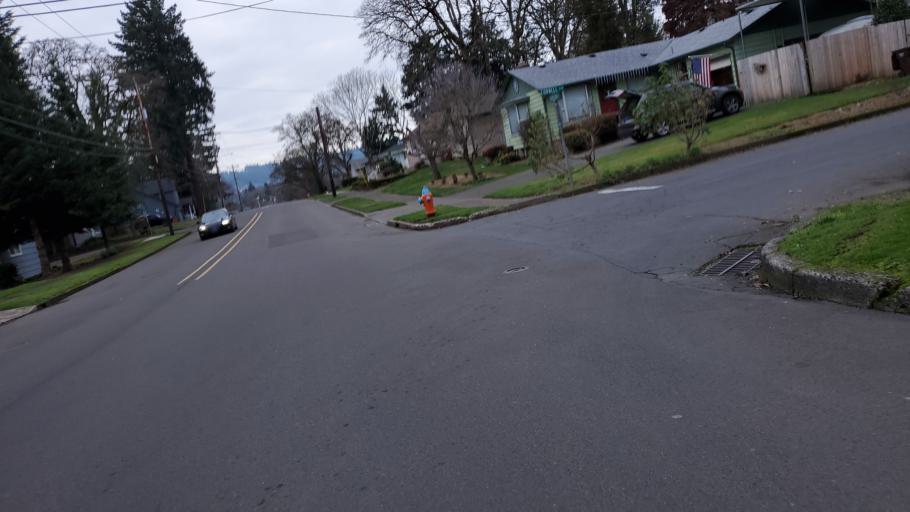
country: US
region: Oregon
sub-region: Clackamas County
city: Gladstone
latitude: 45.3853
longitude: -122.5890
